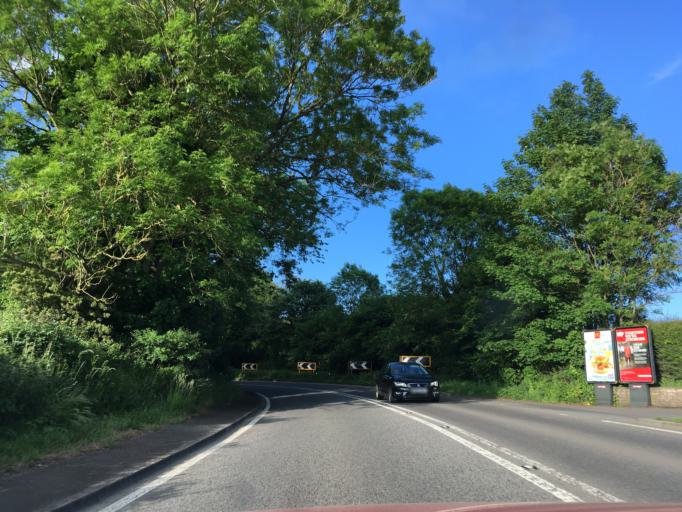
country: GB
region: England
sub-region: North Somerset
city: Churchill
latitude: 51.3239
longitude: -2.7975
